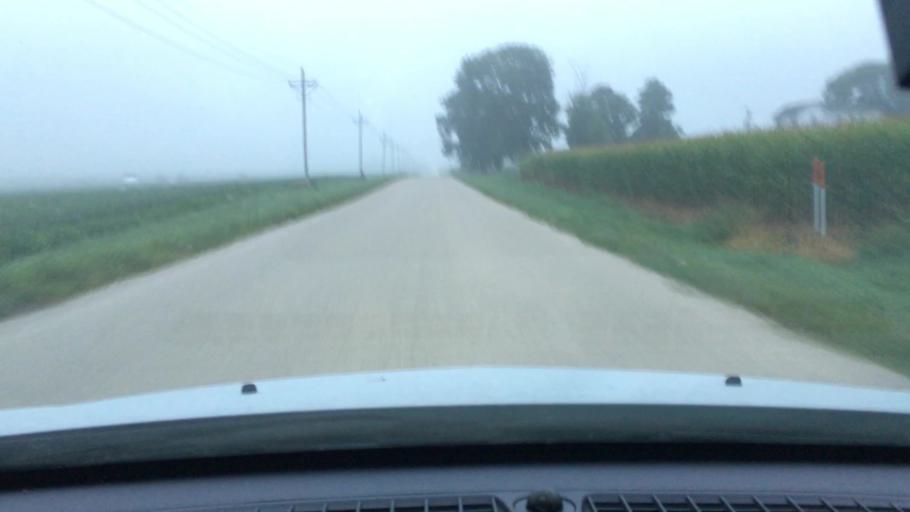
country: US
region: Illinois
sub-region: Ogle County
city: Rochelle
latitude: 41.8985
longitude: -88.9956
